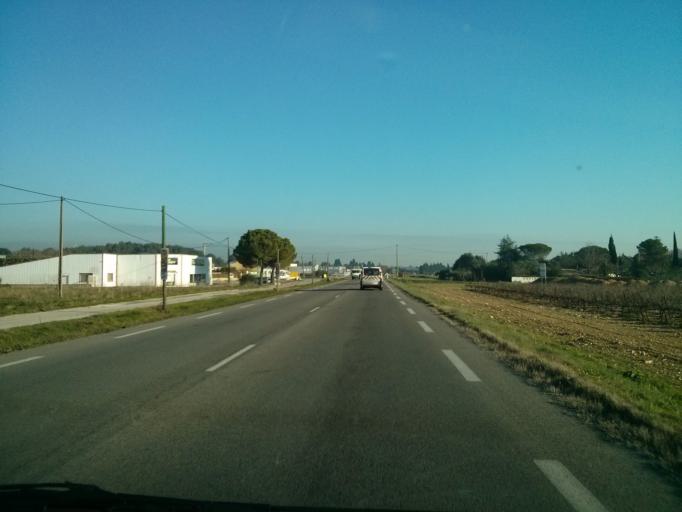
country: FR
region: Languedoc-Roussillon
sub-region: Departement du Gard
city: Vestric-et-Candiac
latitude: 43.7442
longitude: 4.2503
